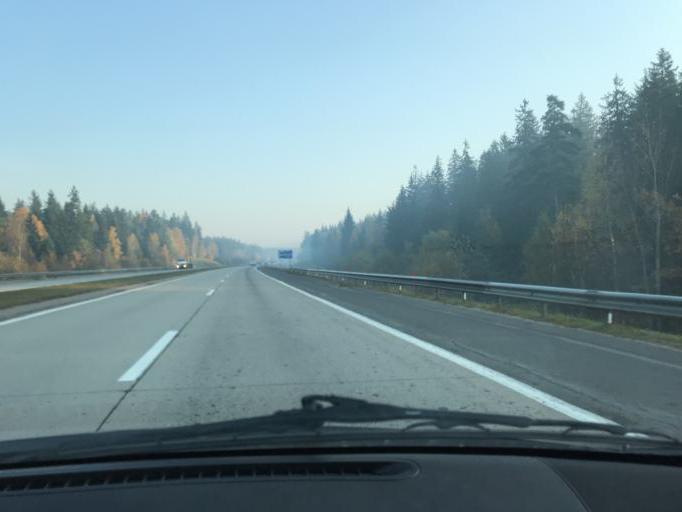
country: BY
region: Minsk
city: Borovlyany
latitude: 54.0182
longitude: 27.6631
